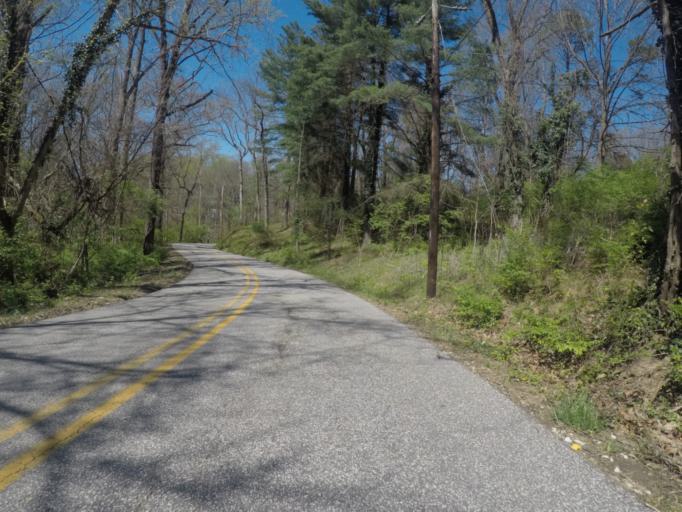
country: US
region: West Virginia
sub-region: Cabell County
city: Pea Ridge
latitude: 38.4166
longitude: -82.3182
